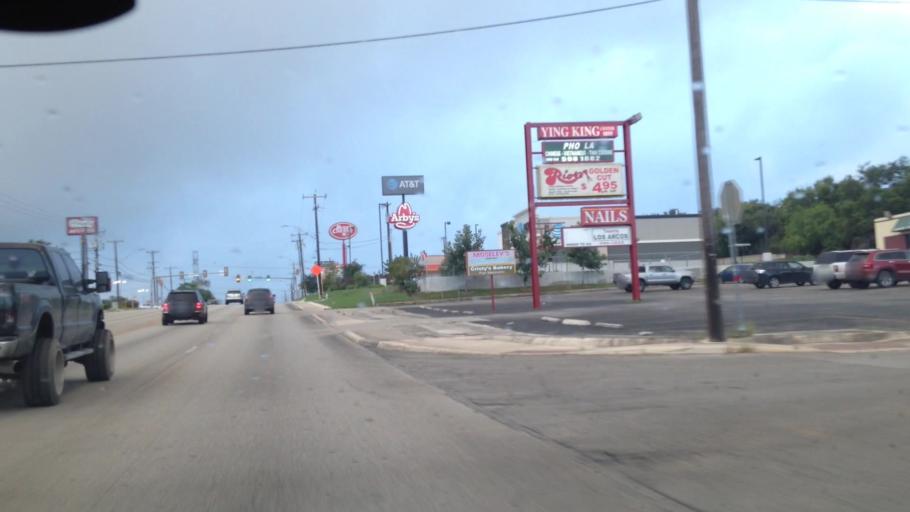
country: US
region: Texas
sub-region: Bexar County
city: Live Oak
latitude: 29.5663
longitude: -98.3876
